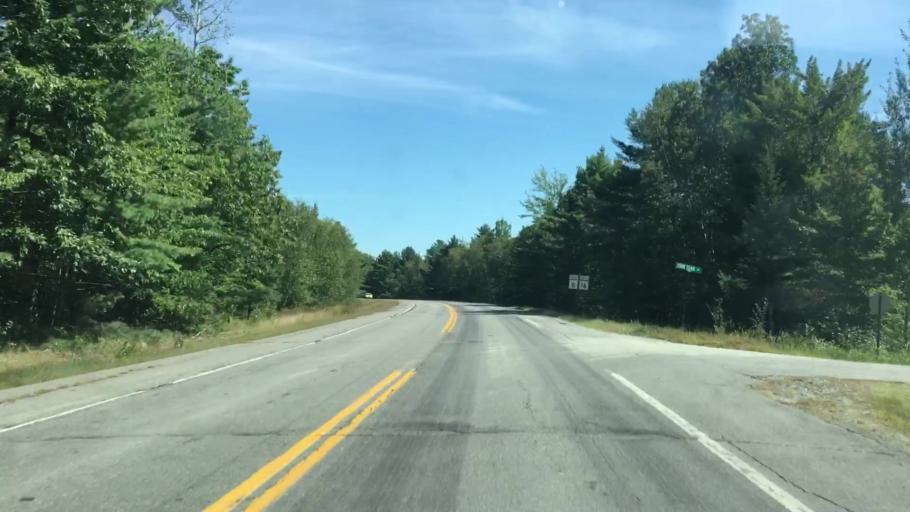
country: US
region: Maine
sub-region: Piscataquis County
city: Milo
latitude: 45.2298
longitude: -68.9522
